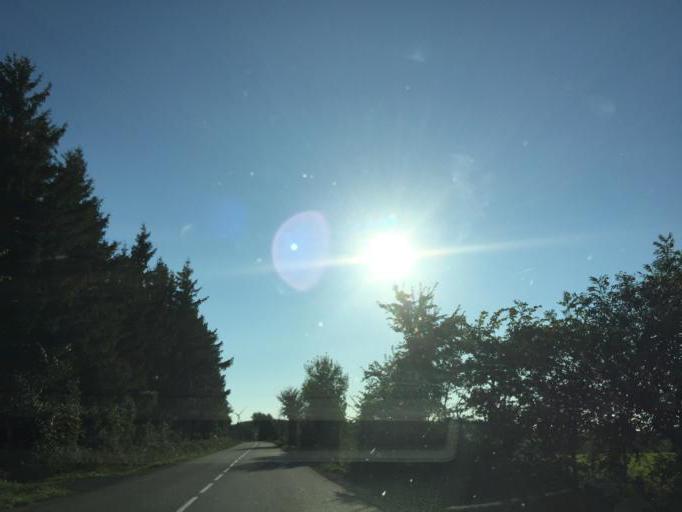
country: FR
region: Midi-Pyrenees
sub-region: Departement de l'Aveyron
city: Salles-Curan
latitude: 44.1621
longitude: 2.8165
